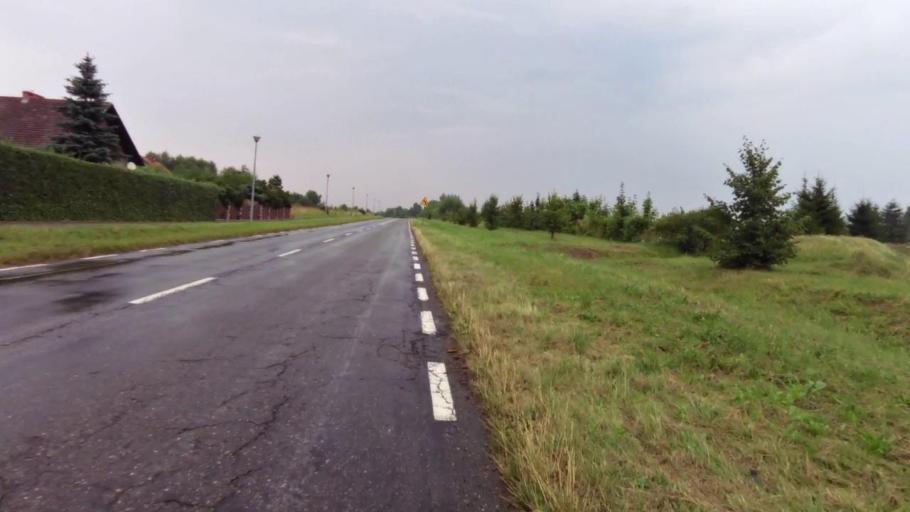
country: PL
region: West Pomeranian Voivodeship
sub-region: Powiat stargardzki
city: Insko
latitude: 53.4411
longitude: 15.5588
